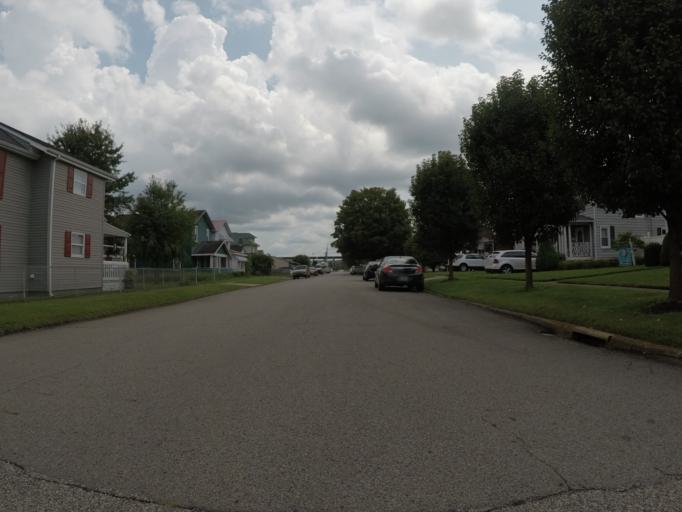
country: US
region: West Virginia
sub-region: Wayne County
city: Kenova
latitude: 38.4009
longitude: -82.5801
